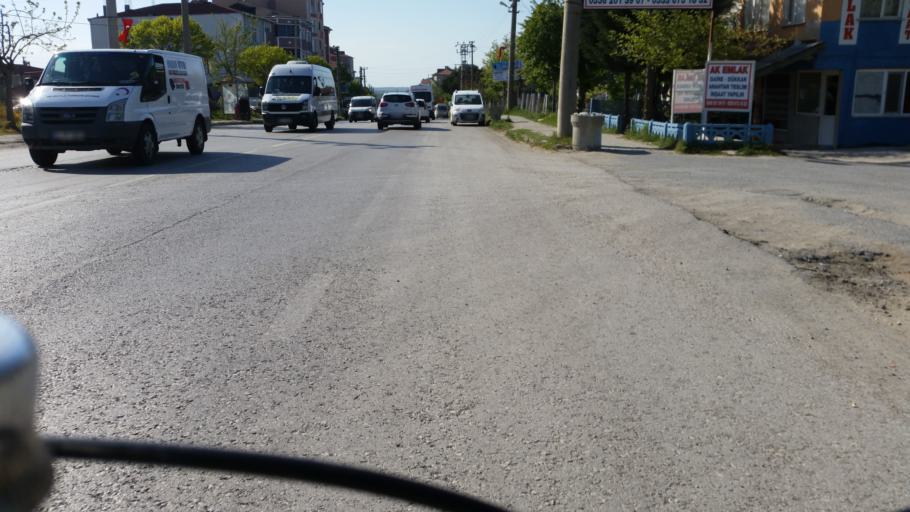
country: TR
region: Tekirdag
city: Cerkezkoey
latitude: 41.3572
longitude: 27.9519
